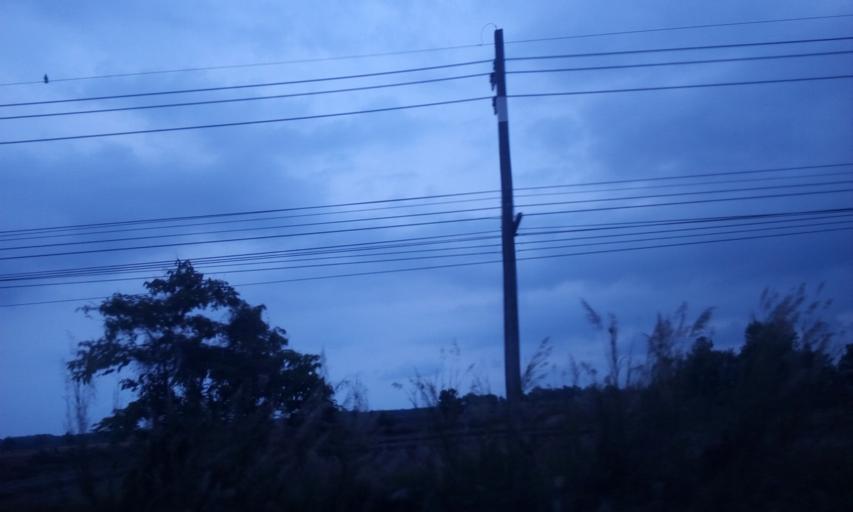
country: TH
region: Chanthaburi
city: Khlung
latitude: 12.4352
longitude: 102.3070
